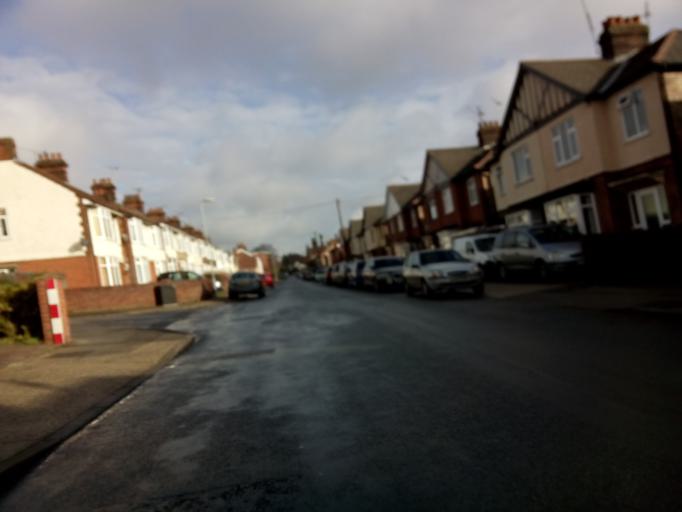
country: GB
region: England
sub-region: Suffolk
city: Ipswich
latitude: 52.0702
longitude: 1.1302
